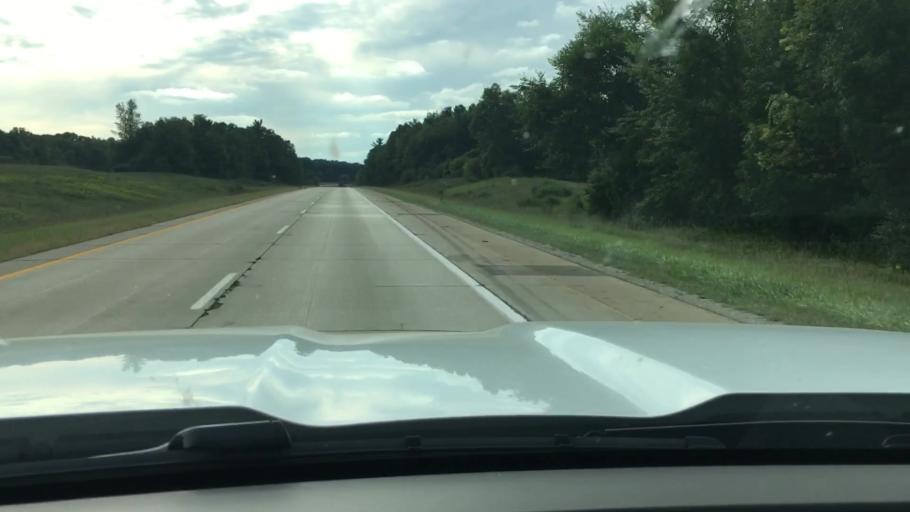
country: US
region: Michigan
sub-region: Lapeer County
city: Lapeer
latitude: 43.0091
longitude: -83.2021
